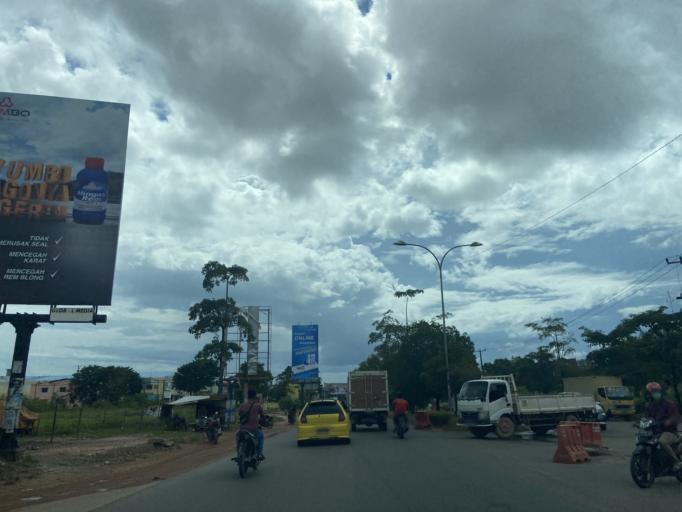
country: SG
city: Singapore
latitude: 1.0407
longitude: 103.9850
